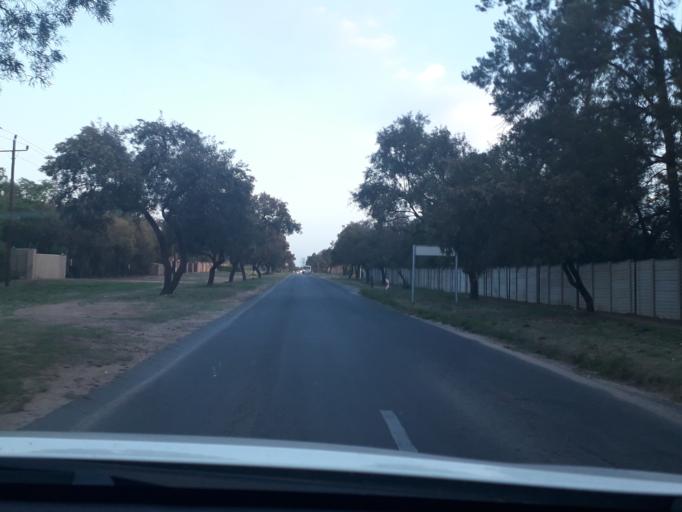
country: ZA
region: Gauteng
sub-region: City of Johannesburg Metropolitan Municipality
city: Diepsloot
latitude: -25.9839
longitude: 28.0457
